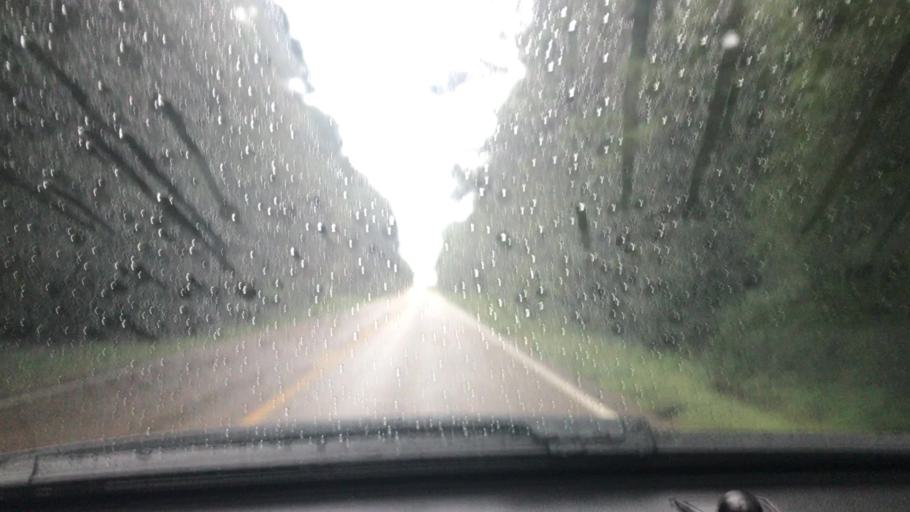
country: US
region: Mississippi
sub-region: Pike County
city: Summit
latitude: 31.2905
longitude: -90.4908
